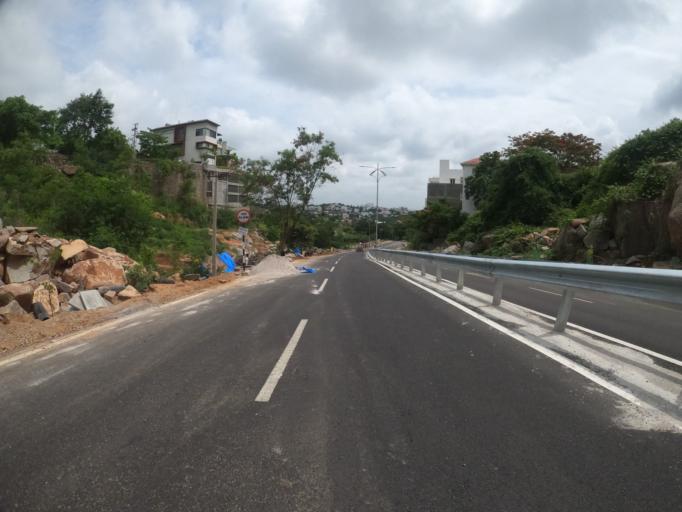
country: IN
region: Telangana
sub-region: Rangareddi
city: Kukatpalli
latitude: 17.4205
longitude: 78.3981
